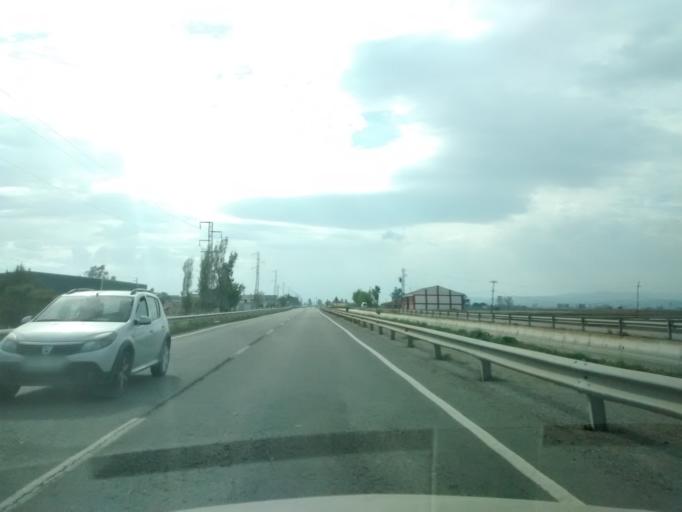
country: ES
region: Catalonia
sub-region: Provincia de Tarragona
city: Deltebre
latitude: 40.7259
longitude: 0.7131
